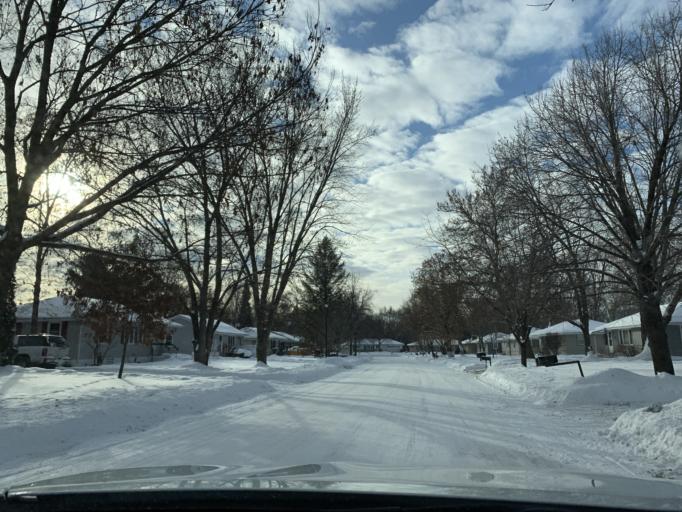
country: US
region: Minnesota
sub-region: Anoka County
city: Blaine
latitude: 45.1763
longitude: -93.2880
